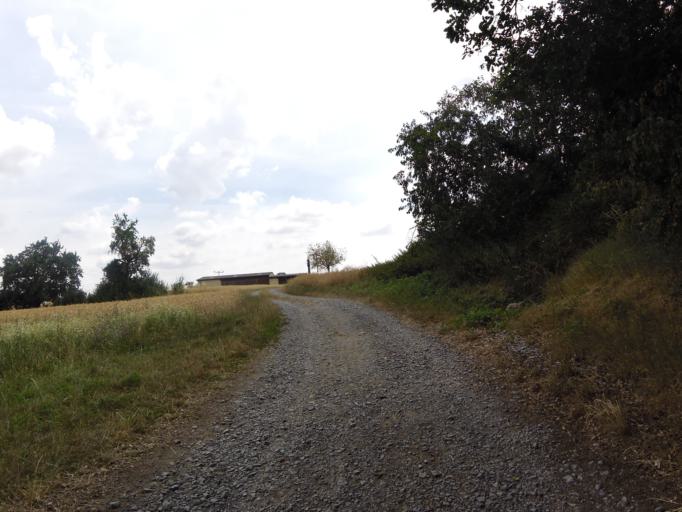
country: DE
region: Bavaria
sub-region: Regierungsbezirk Unterfranken
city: Gerbrunn
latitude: 49.7748
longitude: 9.9823
